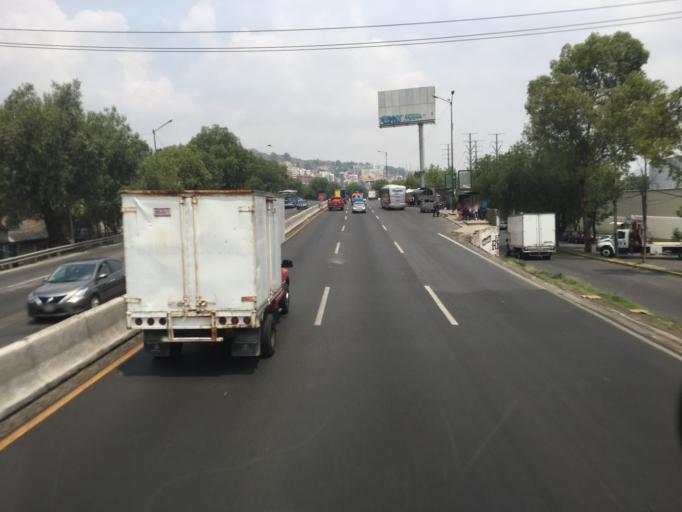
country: MX
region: Mexico
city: Tlalnepantla
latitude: 19.5623
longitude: -99.2018
